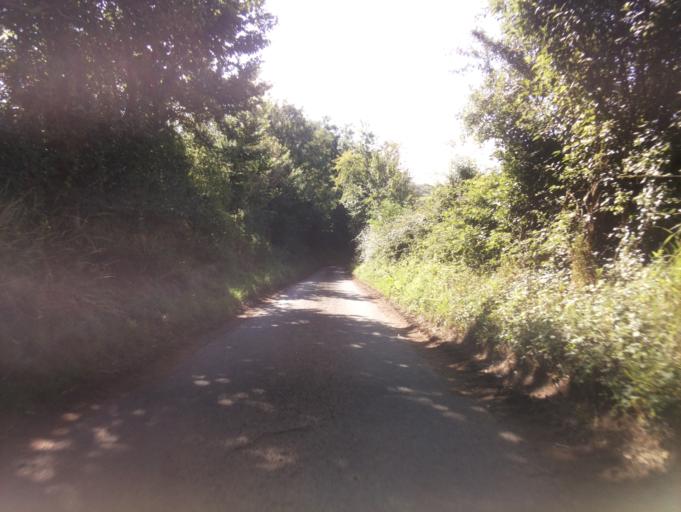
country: GB
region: England
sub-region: Herefordshire
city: Brockhampton
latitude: 51.9717
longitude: -2.5720
